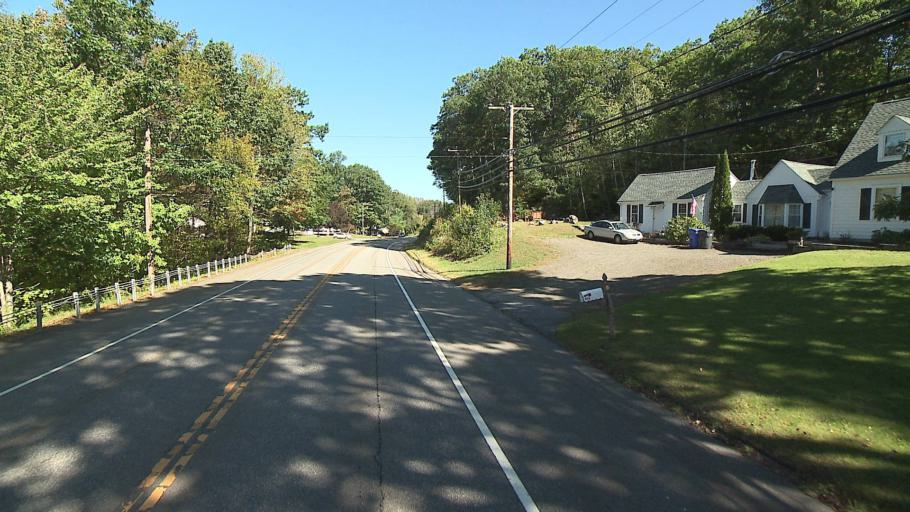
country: US
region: Connecticut
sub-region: Litchfield County
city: Litchfield
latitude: 41.7702
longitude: -73.1743
